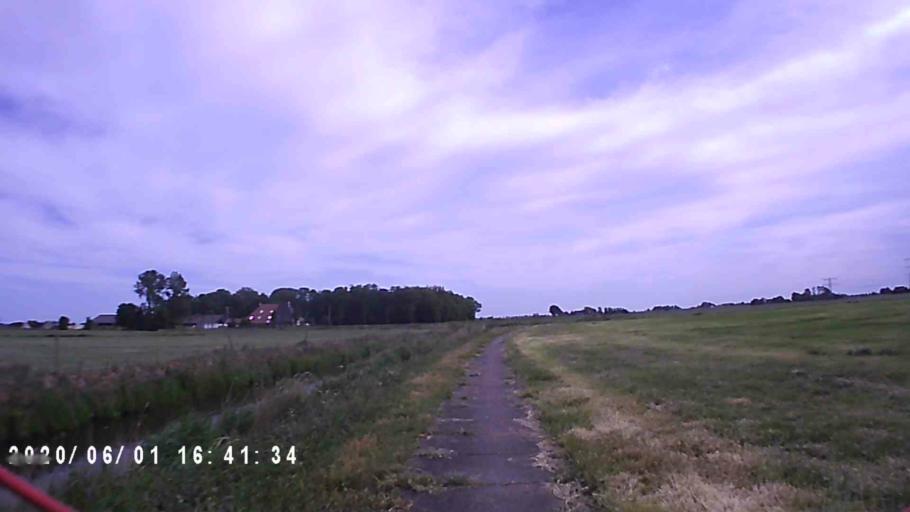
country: NL
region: Friesland
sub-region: Gemeente Boarnsterhim
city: Warten
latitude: 53.1841
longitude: 5.8779
